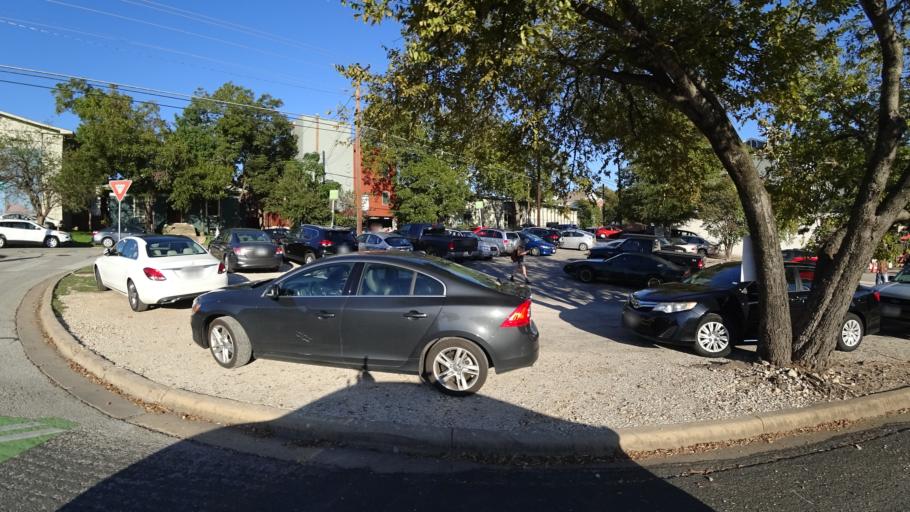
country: US
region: Texas
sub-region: Travis County
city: Austin
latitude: 30.2928
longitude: -97.7359
